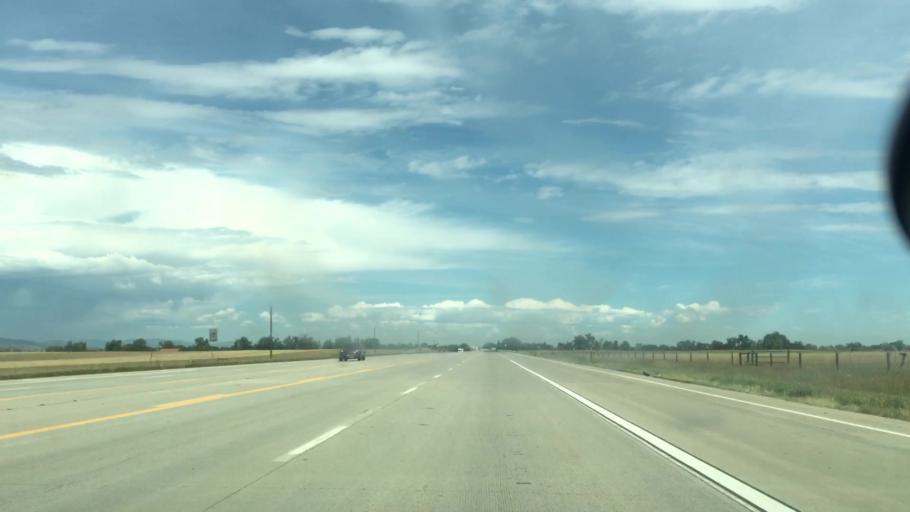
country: US
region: Colorado
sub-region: Boulder County
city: Longmont
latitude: 40.2191
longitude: -105.1023
